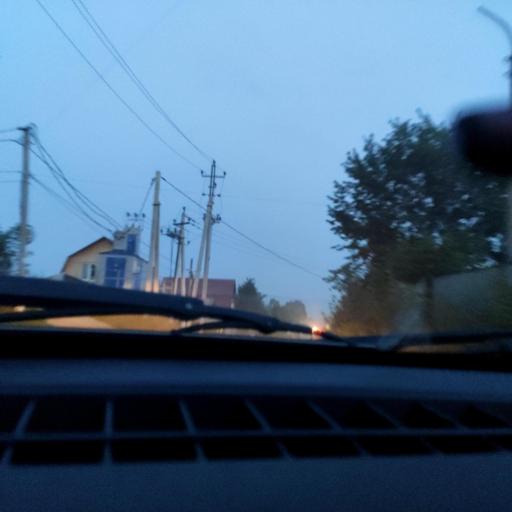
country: RU
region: Bashkortostan
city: Ufa
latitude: 54.7056
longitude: 55.9546
